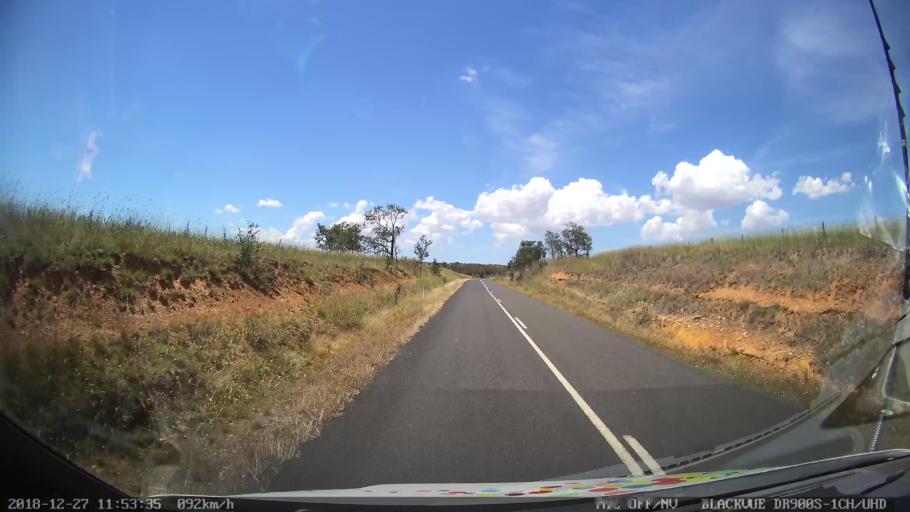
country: AU
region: New South Wales
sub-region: Blayney
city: Blayney
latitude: -33.6639
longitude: 149.4018
